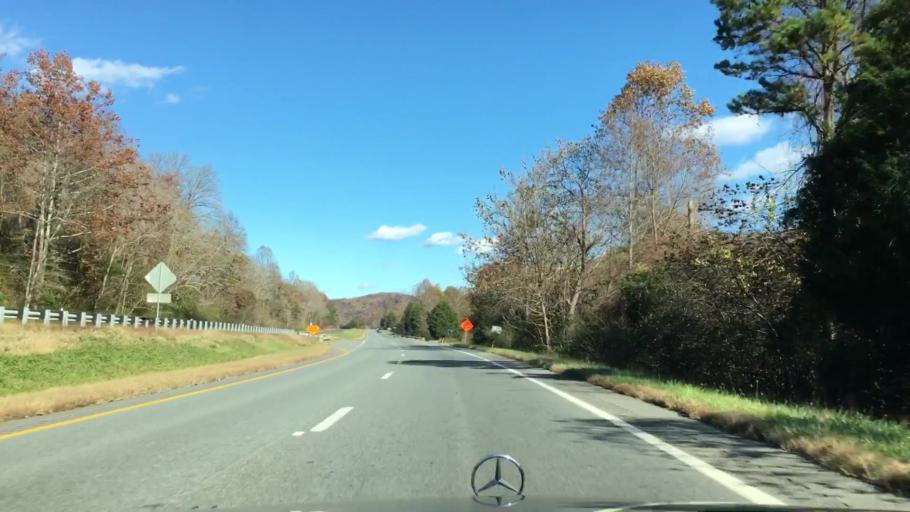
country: US
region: Virginia
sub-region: City of Charlottesville
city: Charlottesville
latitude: 37.9793
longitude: -78.5990
